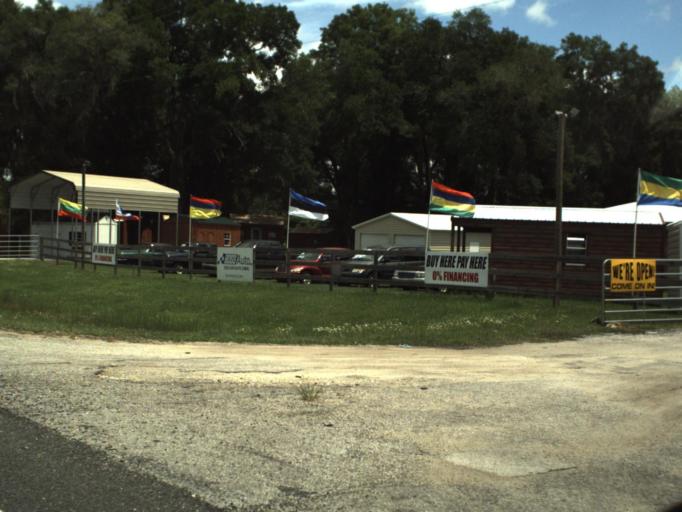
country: US
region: Florida
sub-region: Marion County
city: Ocala
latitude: 29.2475
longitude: -82.1520
